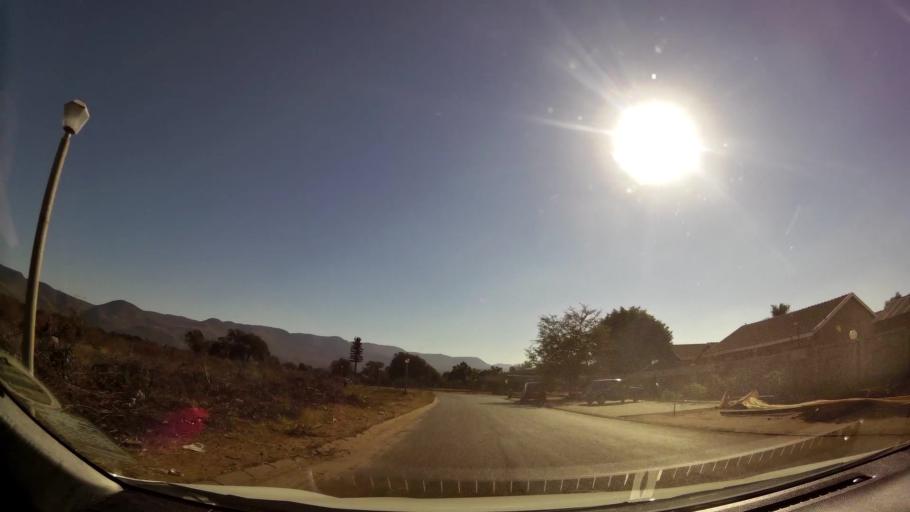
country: ZA
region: Limpopo
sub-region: Waterberg District Municipality
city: Mokopane
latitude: -24.1816
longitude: 28.9974
